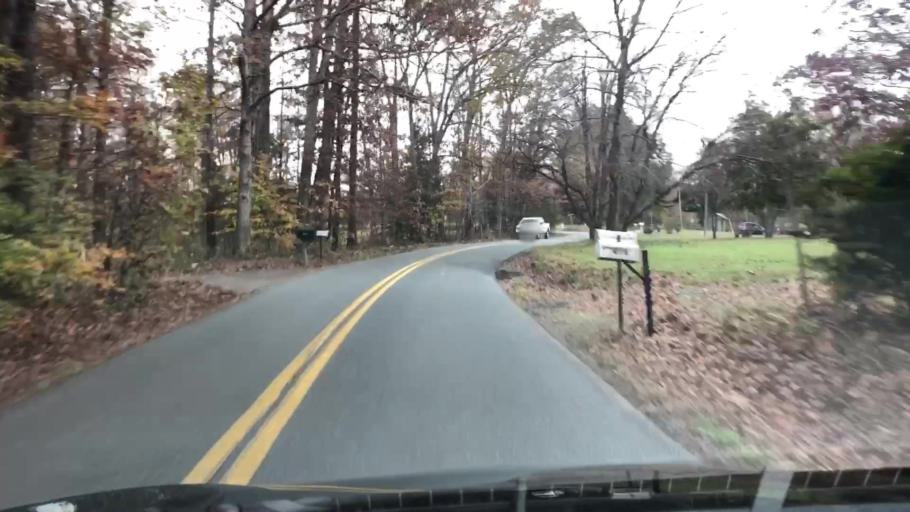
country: US
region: Virginia
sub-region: Stafford County
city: Falmouth
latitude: 38.3885
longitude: -77.5867
